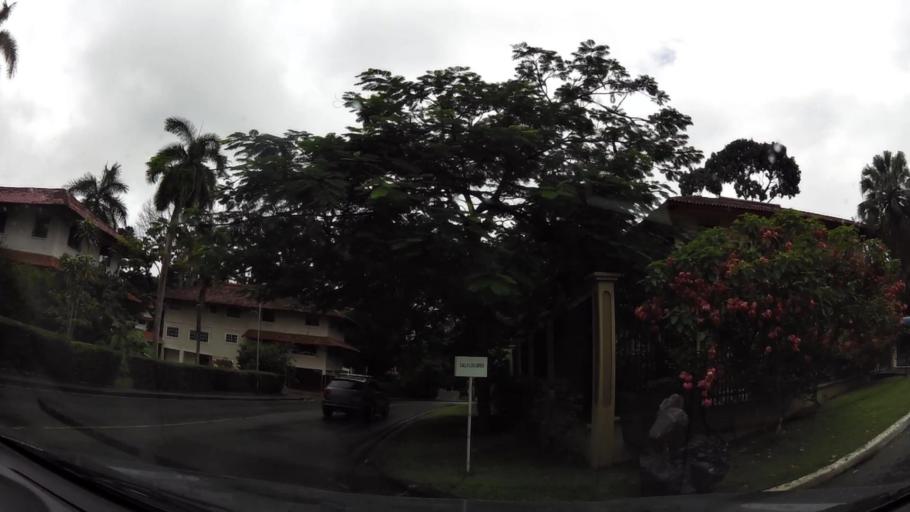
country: PA
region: Panama
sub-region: Distrito de Panama
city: Ancon
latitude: 8.9847
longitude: -79.5582
